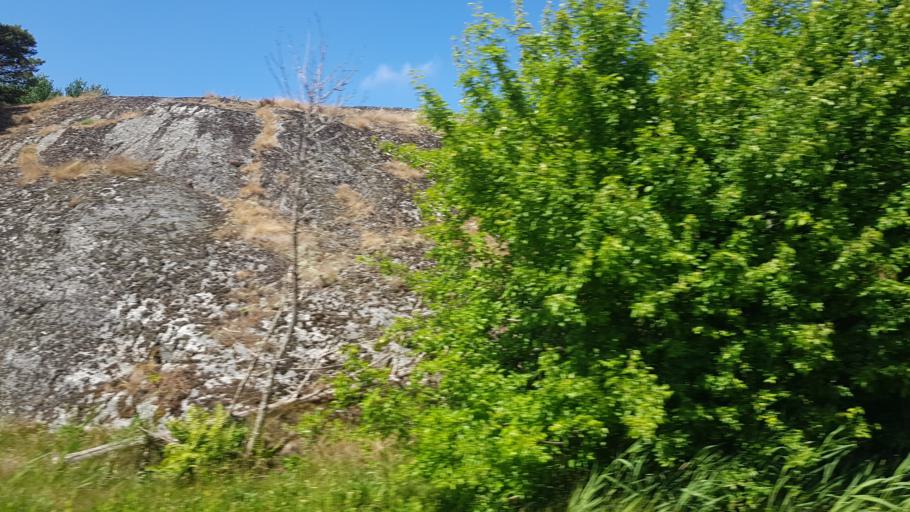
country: SE
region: Vaestra Goetaland
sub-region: Tjorns Kommun
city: Skaerhamn
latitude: 57.9790
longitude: 11.5640
